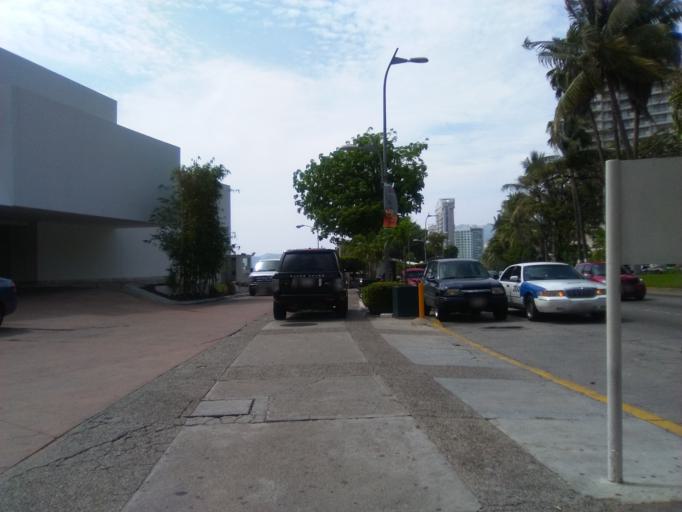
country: MX
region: Guerrero
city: Acapulco de Juarez
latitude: 16.8565
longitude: -99.8663
